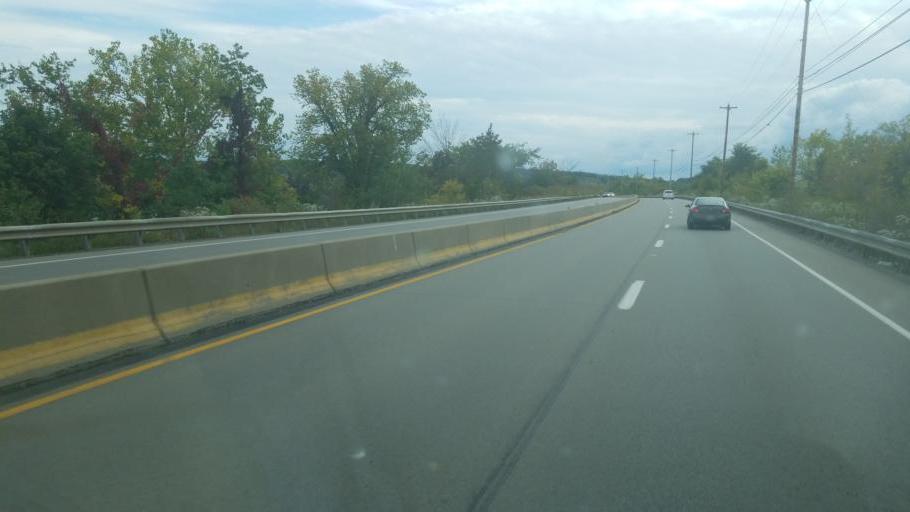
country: US
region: Pennsylvania
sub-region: Mercer County
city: Sharpsville
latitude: 41.2951
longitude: -80.4254
